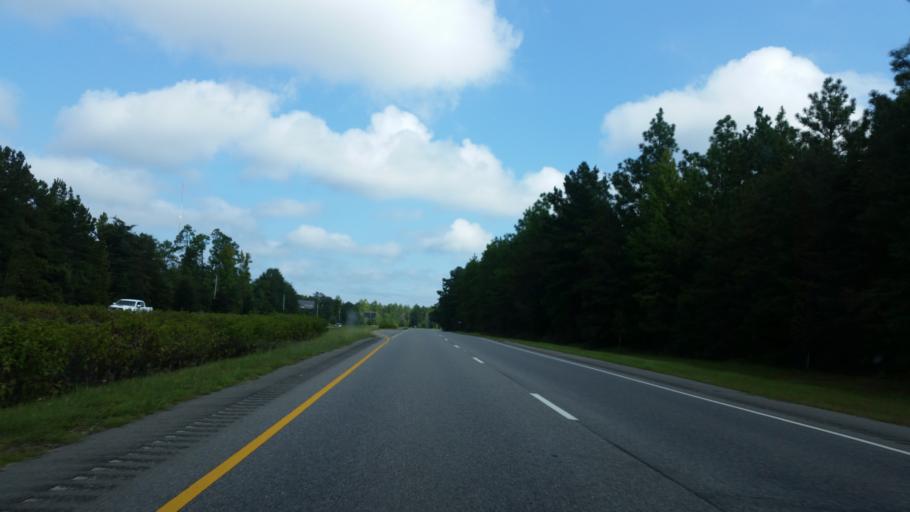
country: US
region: Alabama
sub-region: Baldwin County
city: Bay Minette
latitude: 30.9310
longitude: -87.7691
